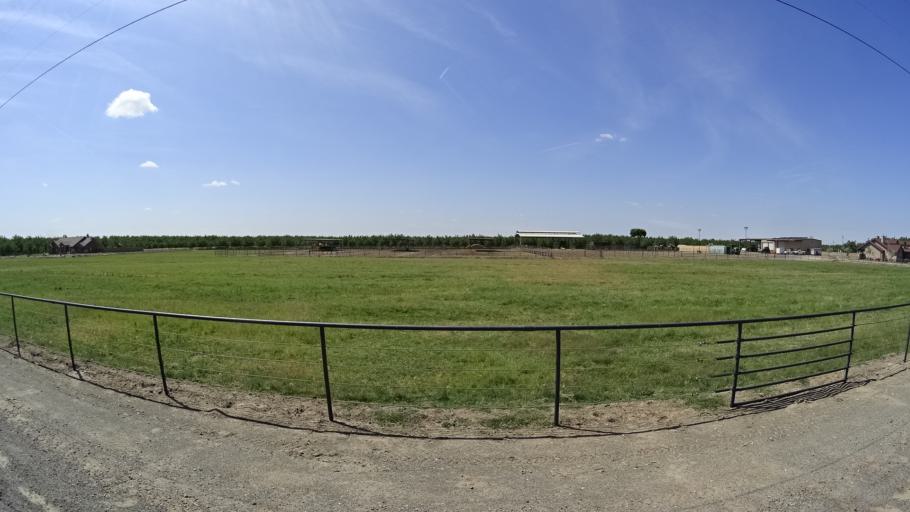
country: US
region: California
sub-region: Kings County
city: Armona
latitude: 36.2694
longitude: -119.7022
